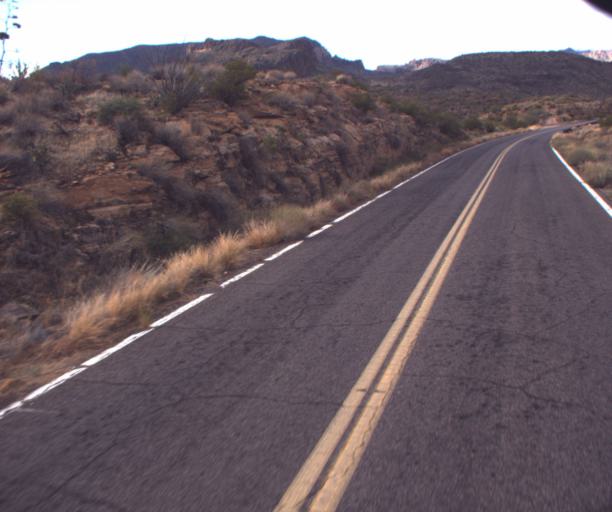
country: US
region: Arizona
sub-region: Pinal County
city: Apache Junction
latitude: 33.5332
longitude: -111.3549
